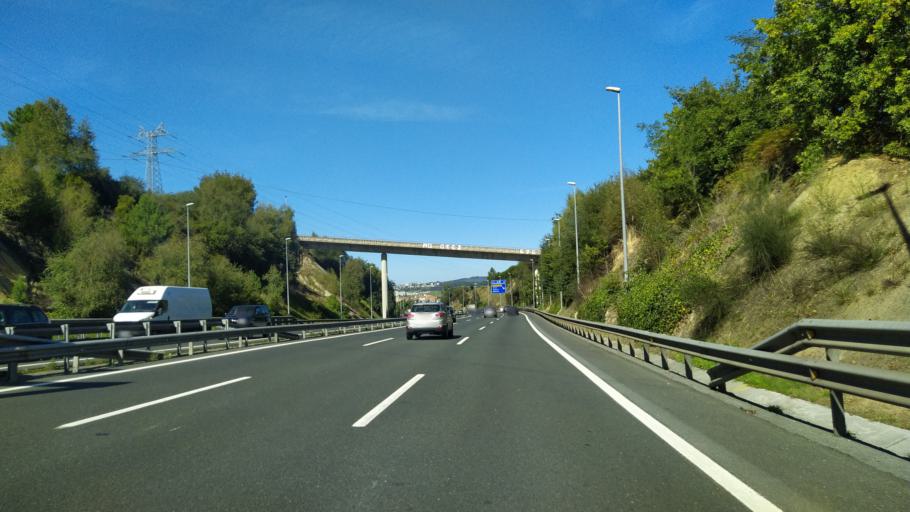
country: ES
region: Basque Country
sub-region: Bizkaia
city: Erandio
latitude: 43.2917
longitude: -2.9433
